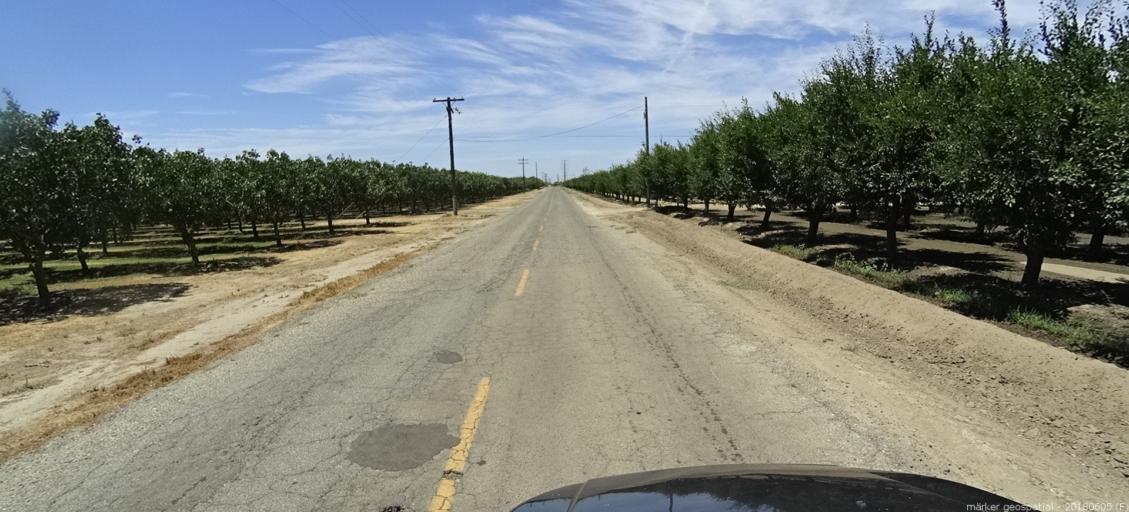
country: US
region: California
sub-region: Madera County
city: Chowchilla
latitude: 37.1200
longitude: -120.3036
